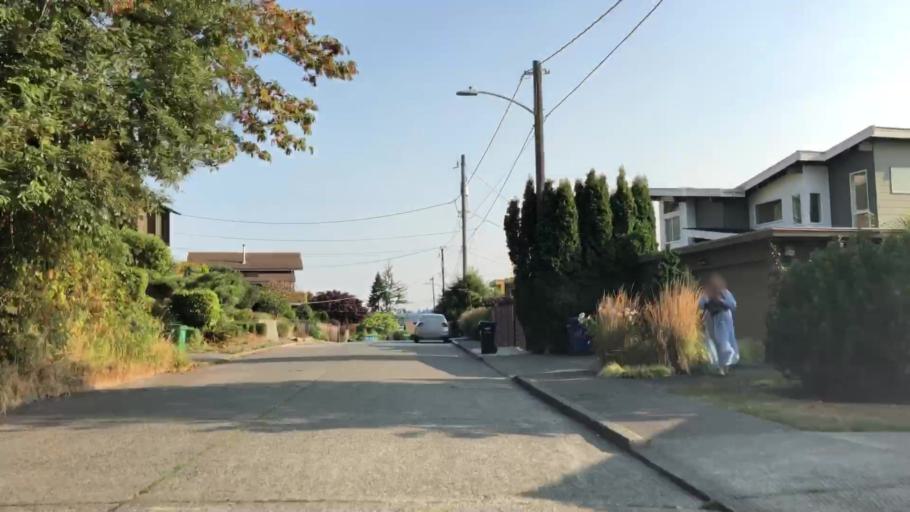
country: US
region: Washington
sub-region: King County
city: Seattle
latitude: 47.6682
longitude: -122.4095
